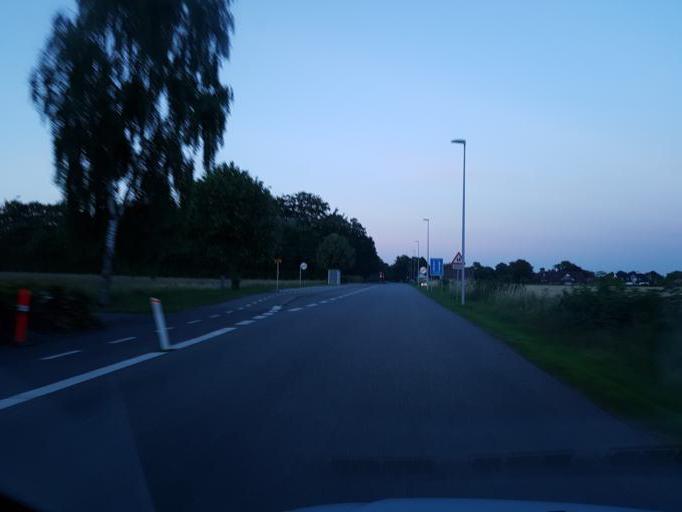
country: DK
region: South Denmark
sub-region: Vejen Kommune
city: Vejen
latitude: 55.4701
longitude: 9.0800
